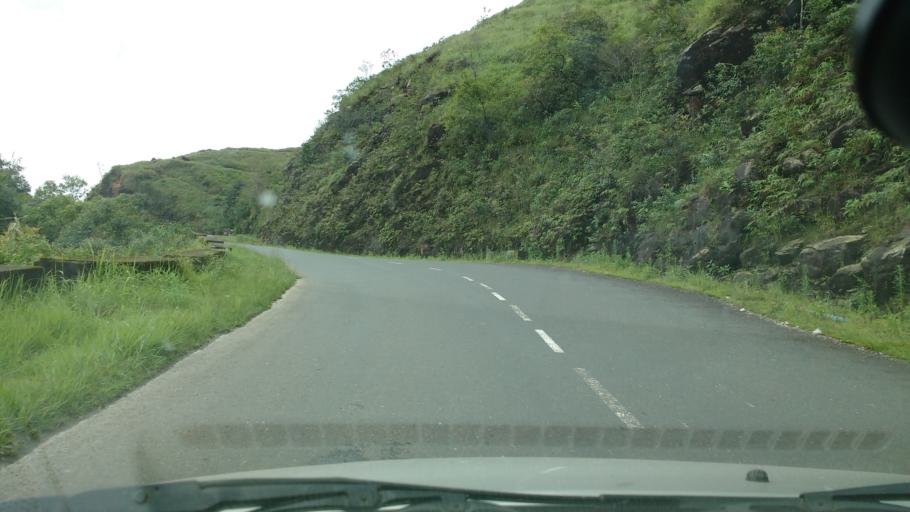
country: IN
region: Meghalaya
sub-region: East Khasi Hills
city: Shillong
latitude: 25.3877
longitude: 91.8717
